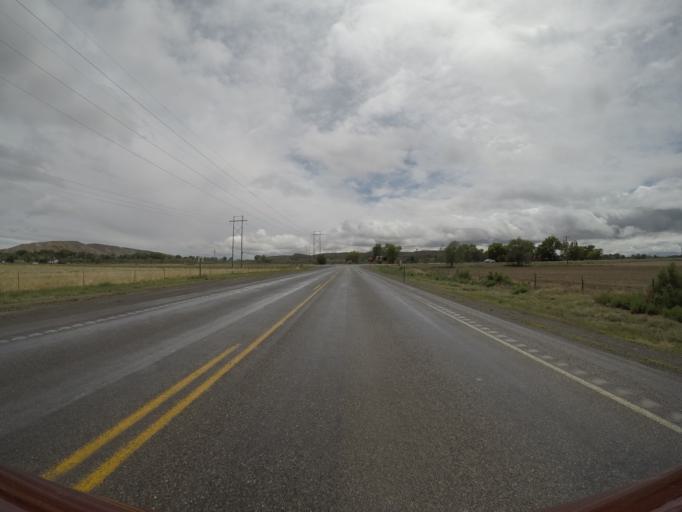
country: US
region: Wyoming
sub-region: Big Horn County
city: Lovell
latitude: 44.8418
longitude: -108.3316
